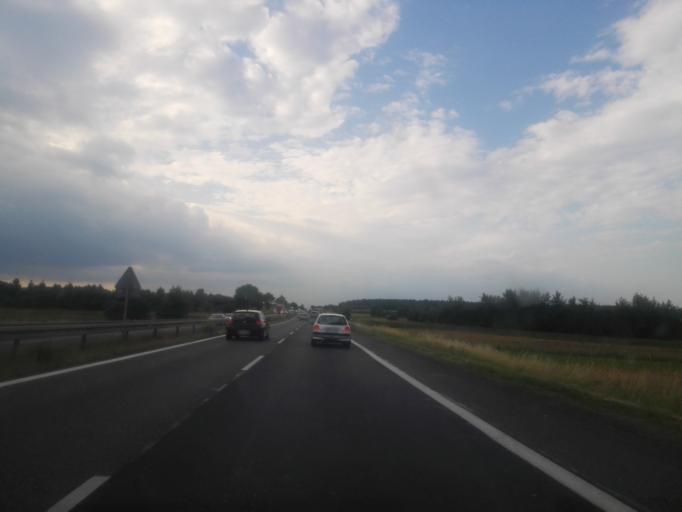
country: PL
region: Silesian Voivodeship
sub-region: Powiat myszkowski
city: Kozieglowy
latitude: 50.5502
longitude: 19.1795
